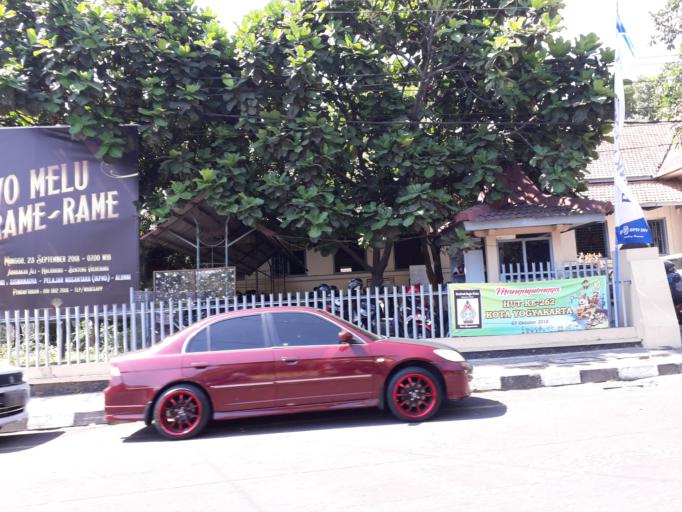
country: ID
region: Daerah Istimewa Yogyakarta
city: Yogyakarta
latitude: -7.7869
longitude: 110.3734
